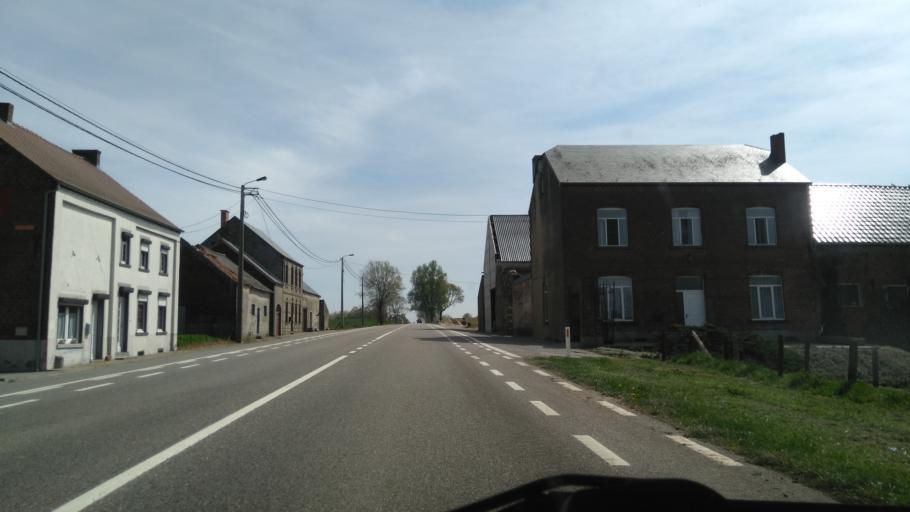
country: BE
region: Wallonia
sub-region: Province du Brabant Wallon
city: Ramillies
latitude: 50.6242
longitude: 4.8764
